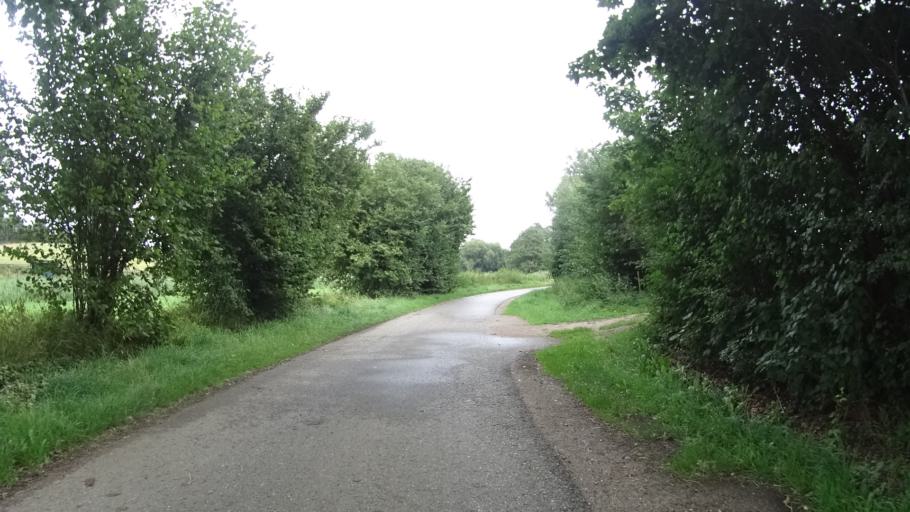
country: DE
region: Schleswig-Holstein
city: Stubben
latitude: 53.7154
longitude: 10.4119
